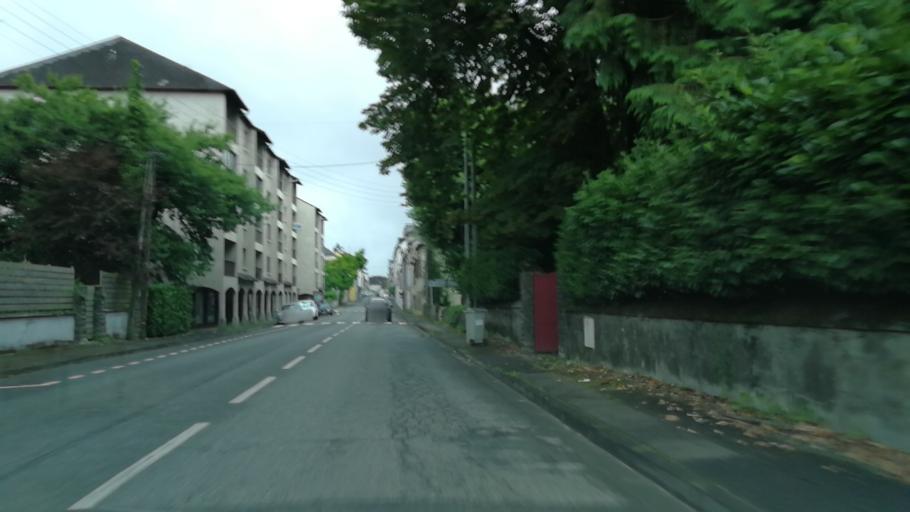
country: FR
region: Aquitaine
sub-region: Departement des Pyrenees-Atlantiques
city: Oloron-Sainte-Marie
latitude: 43.1834
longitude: -0.6084
